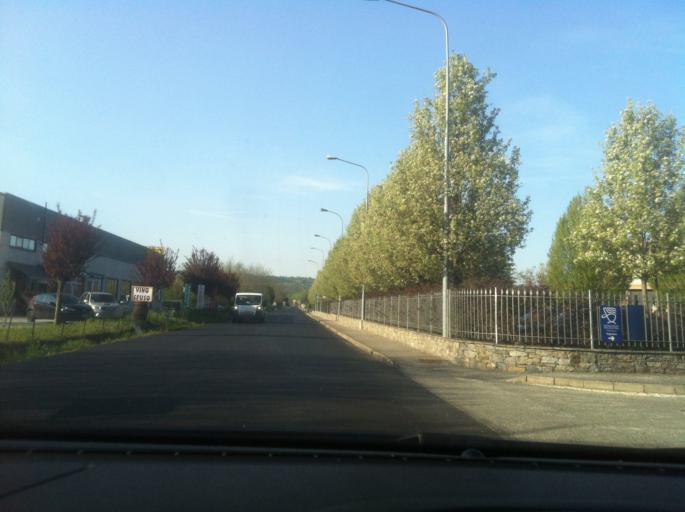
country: IT
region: Piedmont
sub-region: Provincia di Torino
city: Strambino
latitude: 45.3754
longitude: 7.8812
